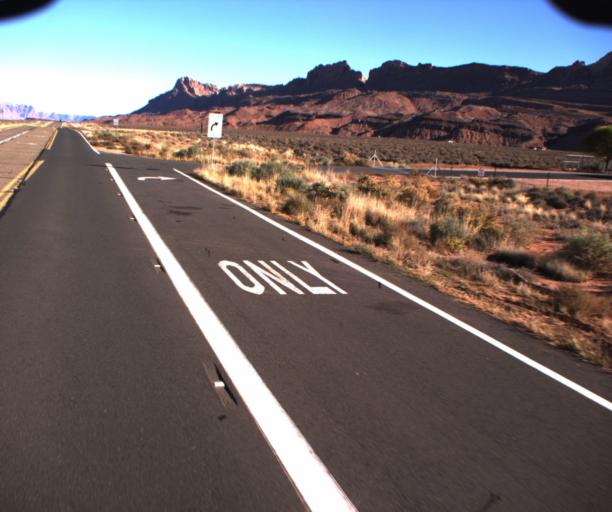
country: US
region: Arizona
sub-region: Coconino County
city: LeChee
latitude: 36.6399
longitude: -111.6521
